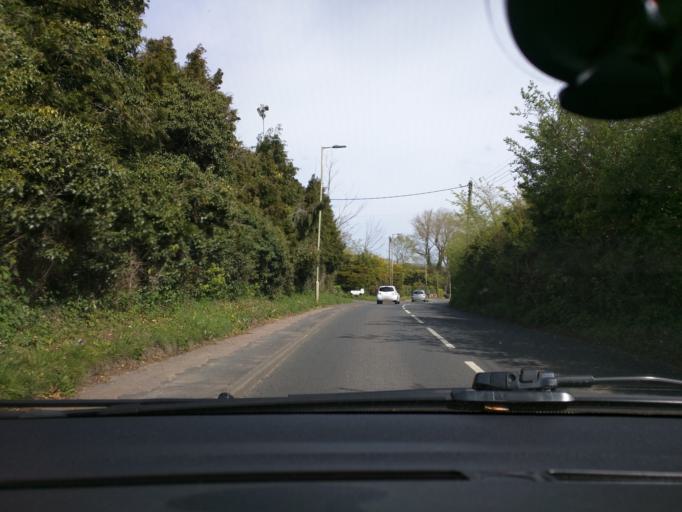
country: GB
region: England
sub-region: Suffolk
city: Leiston
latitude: 52.2115
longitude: 1.5754
